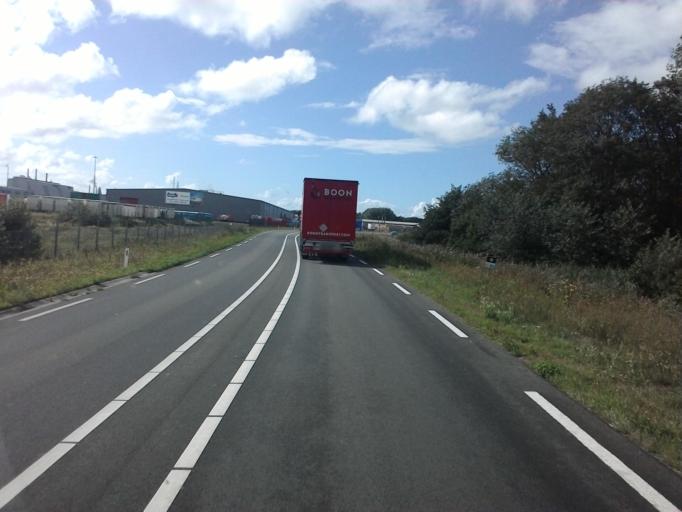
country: NL
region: North Holland
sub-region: Gemeente Beverwijk
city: Beverwijk
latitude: 52.4826
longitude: 4.6349
